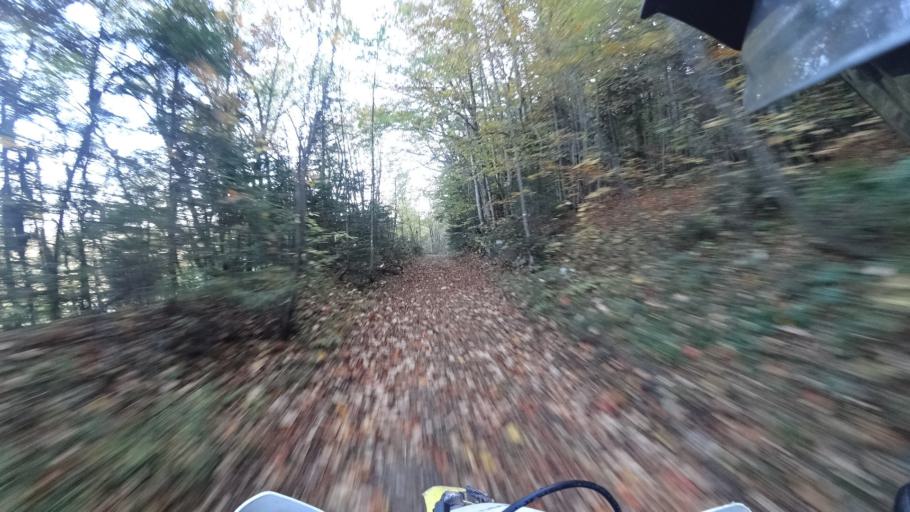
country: HR
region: Karlovacka
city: Plaski
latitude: 44.9586
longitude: 15.4464
